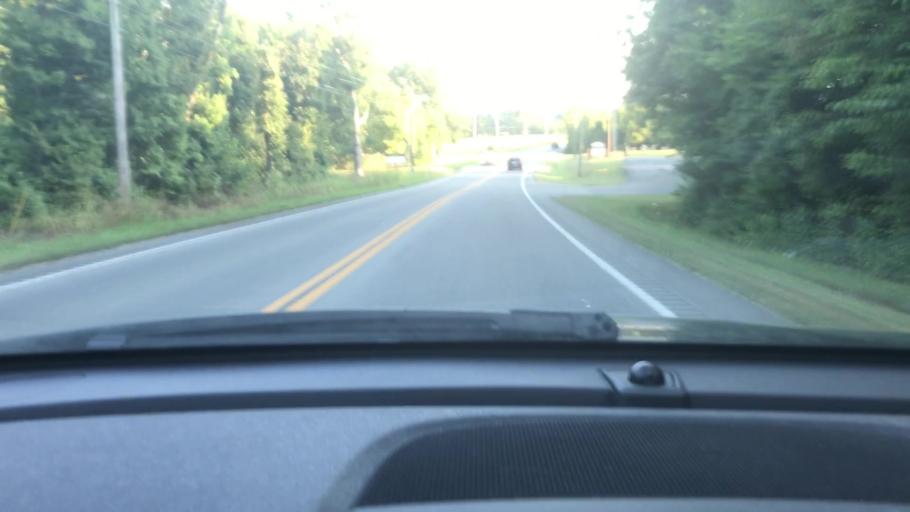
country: US
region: Tennessee
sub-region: Dickson County
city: Charlotte
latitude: 36.1493
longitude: -87.3560
